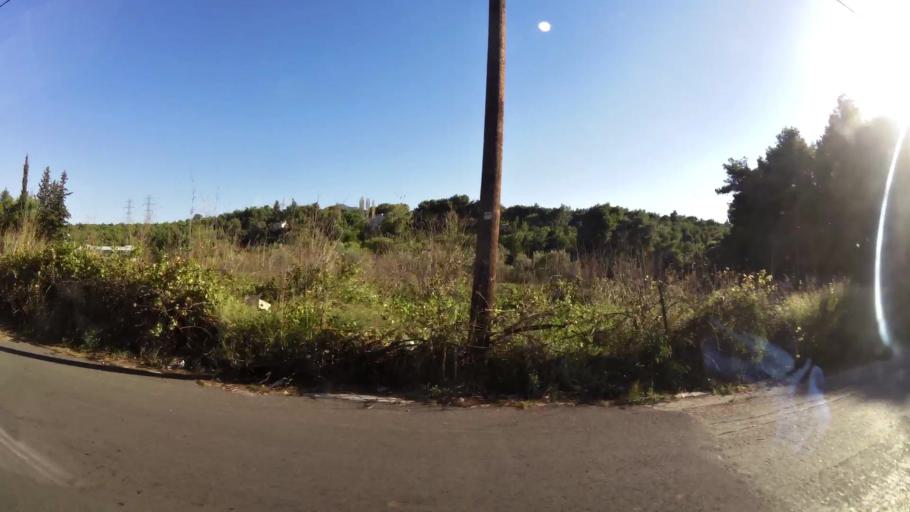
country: GR
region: Attica
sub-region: Nomarchia Anatolikis Attikis
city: Kryoneri
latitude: 38.1268
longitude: 23.8418
